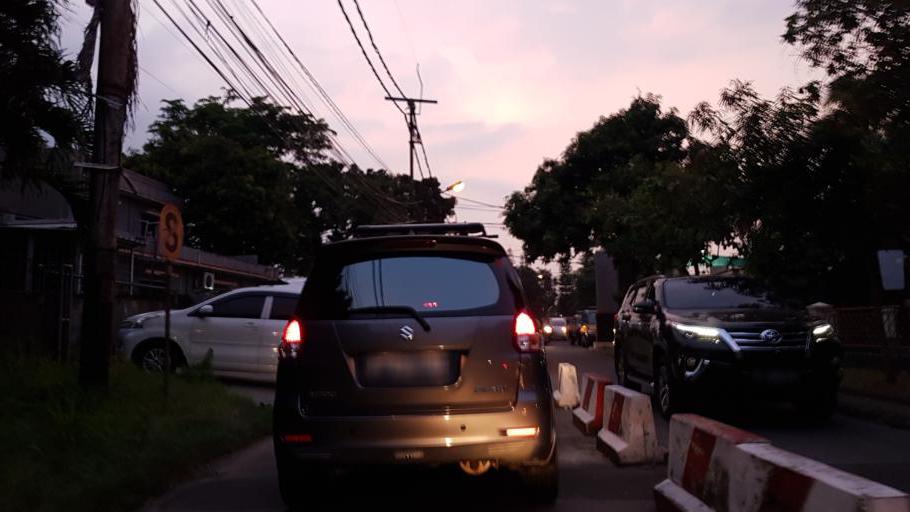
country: ID
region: West Java
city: Pamulang
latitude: -6.3418
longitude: 106.7800
